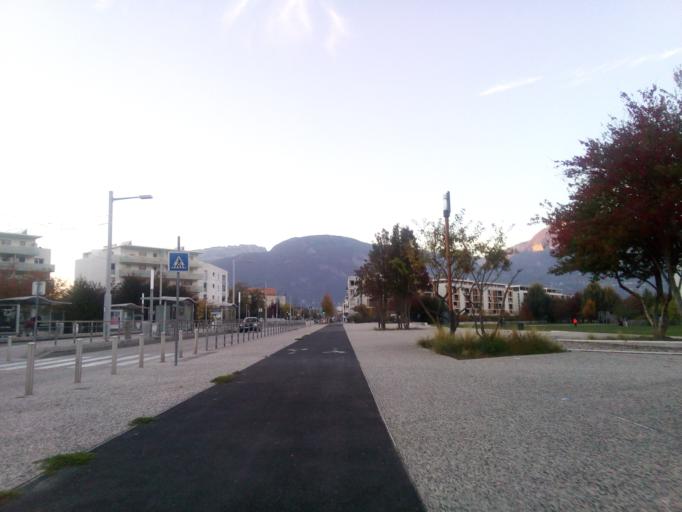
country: FR
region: Rhone-Alpes
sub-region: Departement de l'Isere
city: Saint-Martin-d'Heres
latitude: 45.1748
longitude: 5.7578
